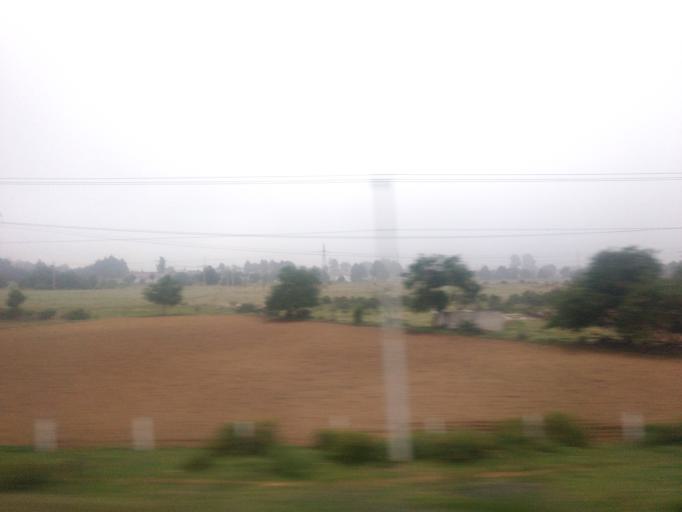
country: MX
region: Veracruz
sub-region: Las Vigas de Ramirez
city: Barrio de San Miguel
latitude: 19.6306
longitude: -97.1229
